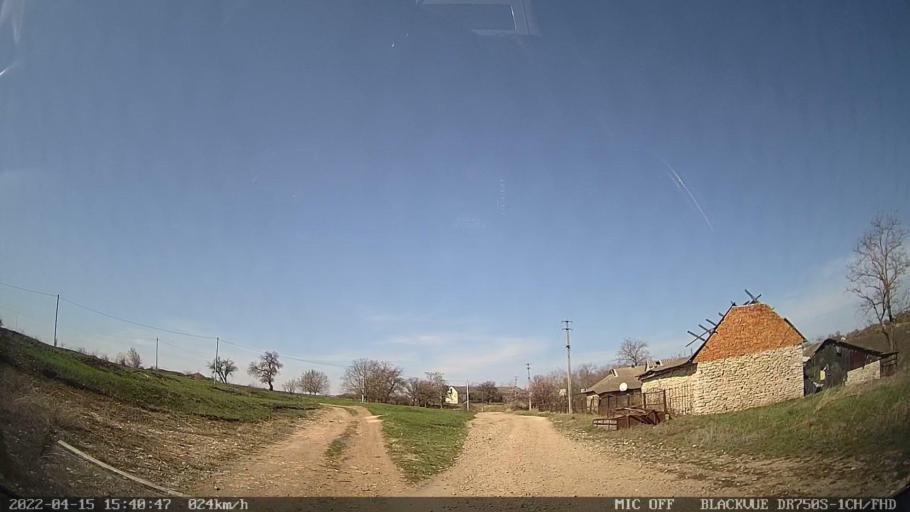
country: MD
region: Raionul Ocnita
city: Otaci
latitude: 48.3570
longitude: 27.9247
